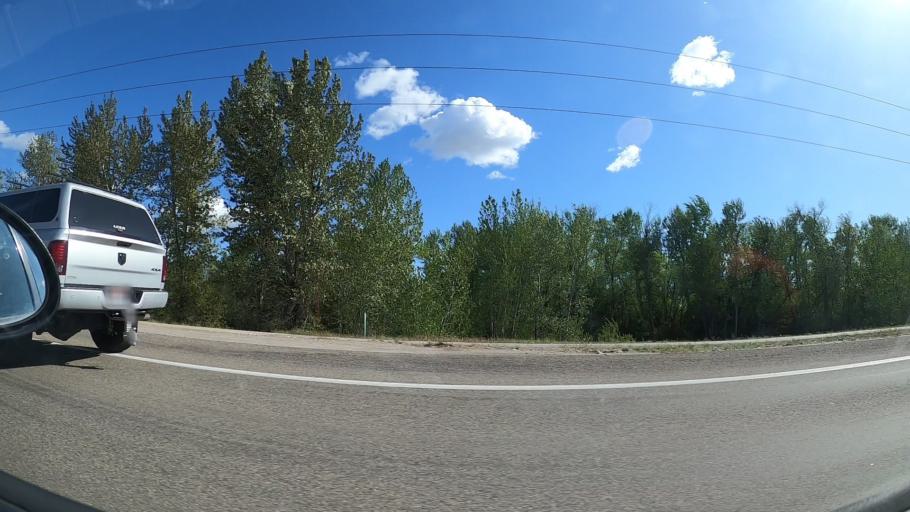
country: US
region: Idaho
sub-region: Ada County
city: Eagle
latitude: 43.6921
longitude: -116.3711
